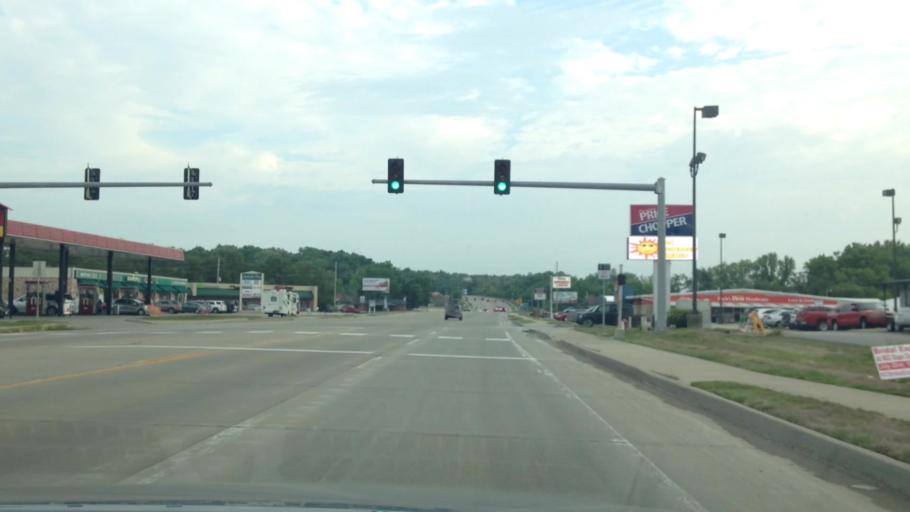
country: US
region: Missouri
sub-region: Clay County
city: Smithville
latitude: 39.3910
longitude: -94.5840
